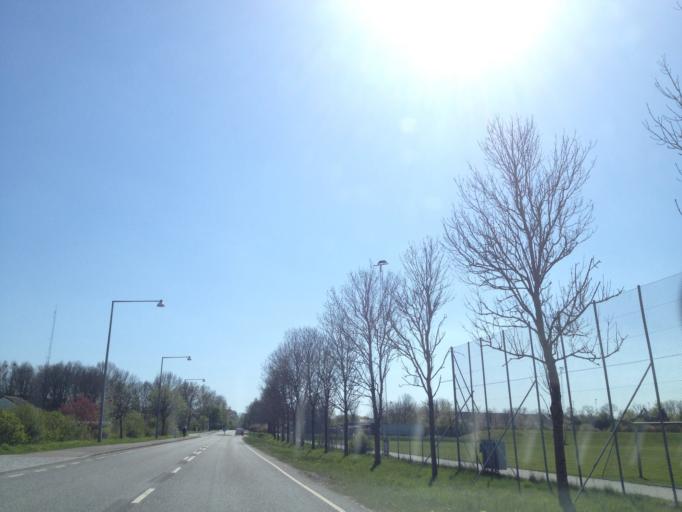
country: DK
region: Zealand
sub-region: Koge Kommune
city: Borup
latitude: 55.5055
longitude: 11.9787
